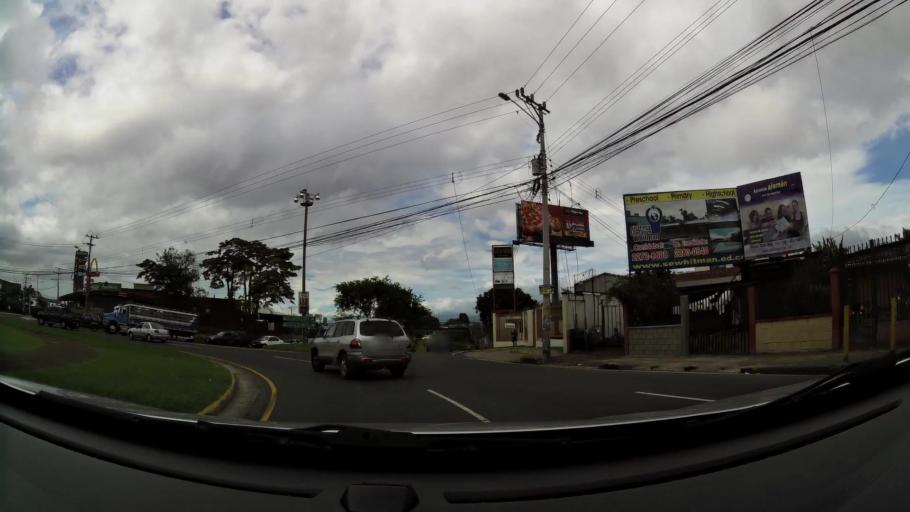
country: CR
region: San Jose
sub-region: Canton de Goicoechea
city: Guadalupe
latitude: 9.9397
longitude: -84.0546
